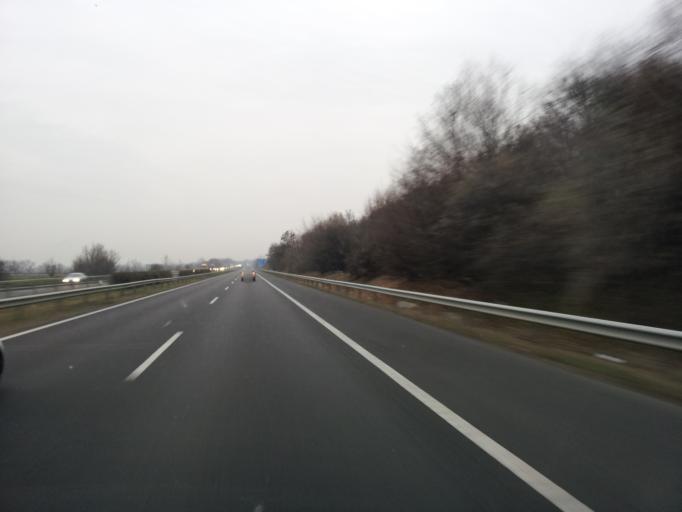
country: HU
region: Pest
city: Tarnok
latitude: 47.3784
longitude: 18.8328
